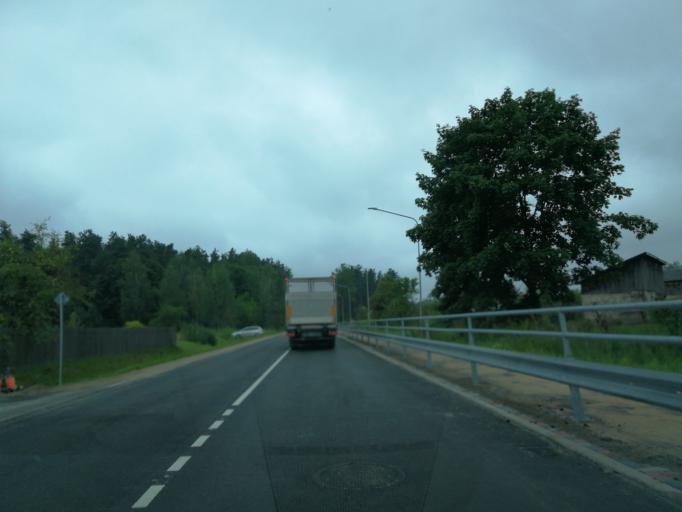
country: LV
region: Livani
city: Livani
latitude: 56.3562
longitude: 26.1856
